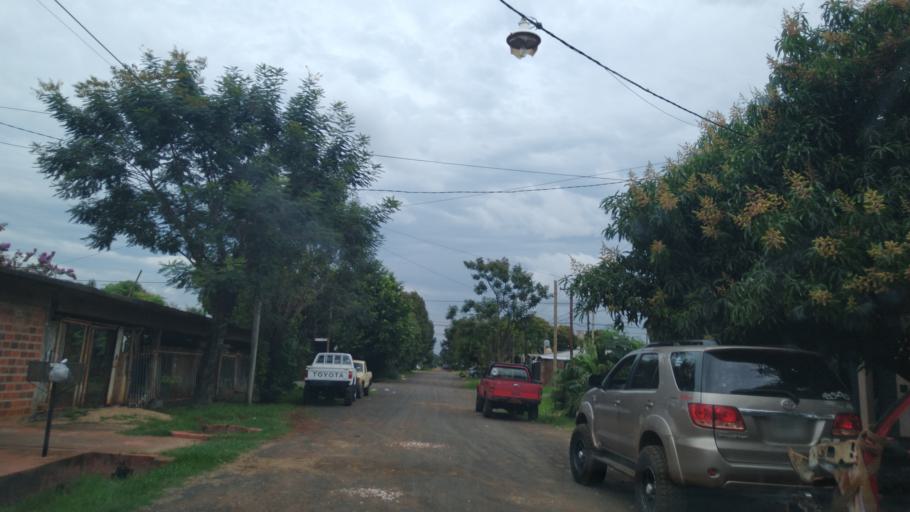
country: AR
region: Misiones
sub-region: Departamento de Capital
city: Posadas
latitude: -27.3773
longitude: -55.9208
